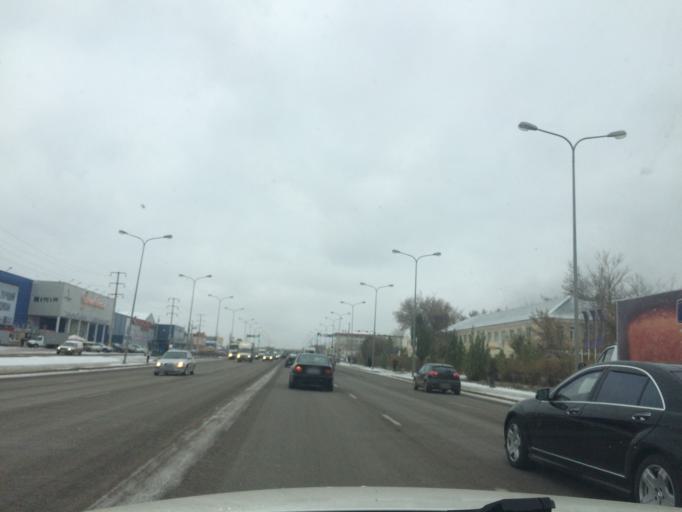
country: KZ
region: Astana Qalasy
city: Astana
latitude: 51.1822
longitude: 71.4584
